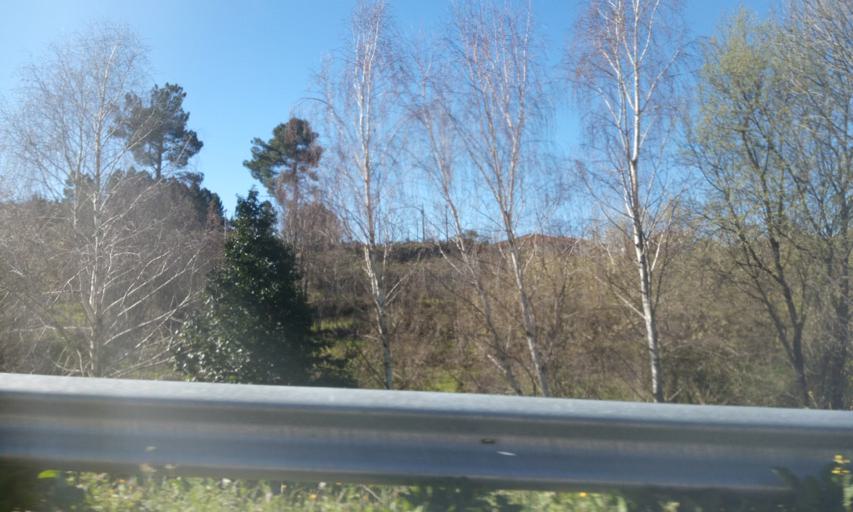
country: PT
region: Guarda
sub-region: Manteigas
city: Manteigas
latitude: 40.5116
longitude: -7.5642
